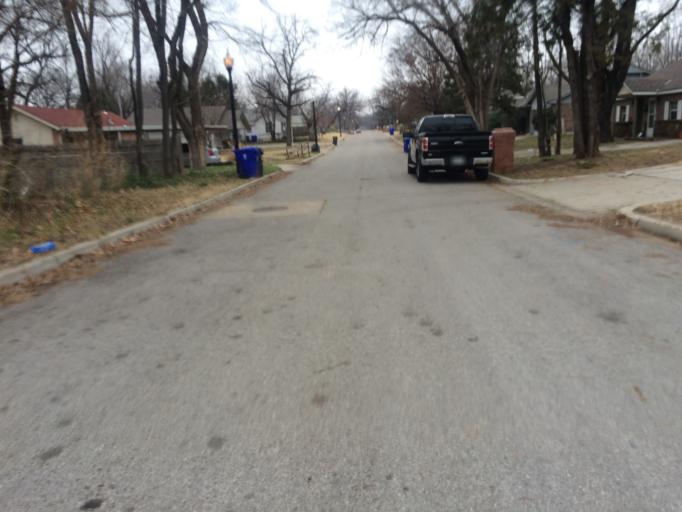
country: US
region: Oklahoma
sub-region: Cleveland County
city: Norman
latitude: 35.2077
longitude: -97.4291
